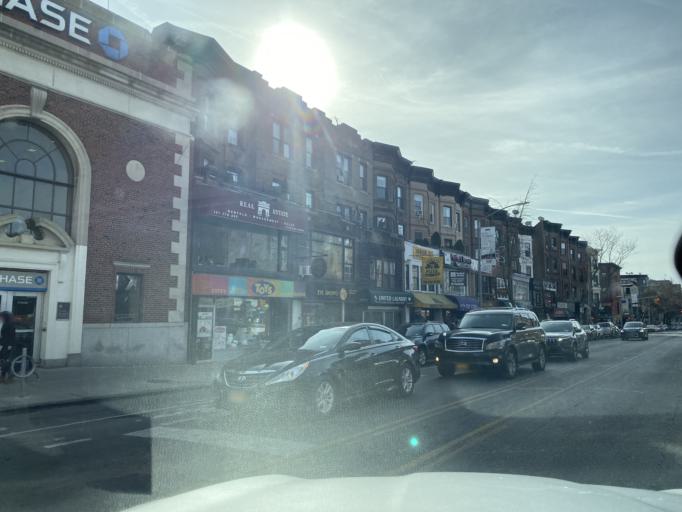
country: US
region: New York
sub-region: Kings County
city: Brooklyn
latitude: 40.6732
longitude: -73.9764
